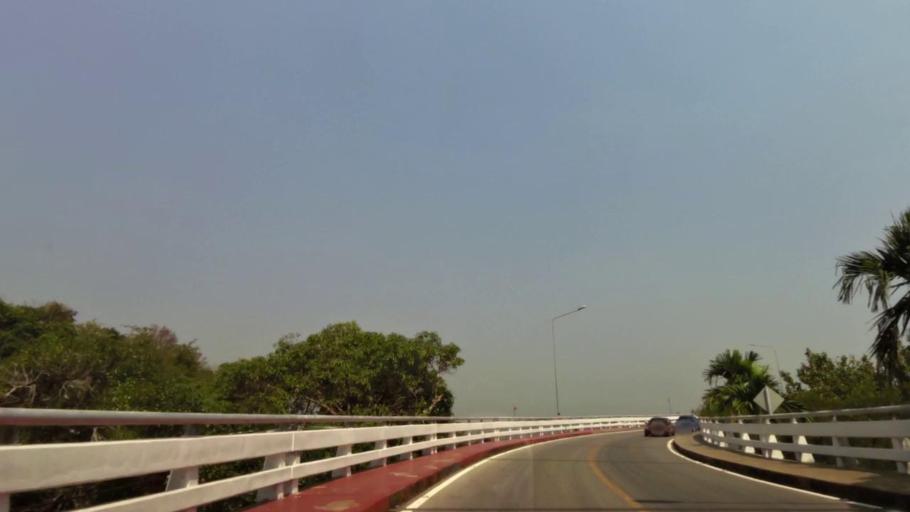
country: TH
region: Chanthaburi
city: Tha Mai
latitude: 12.5387
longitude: 101.9473
